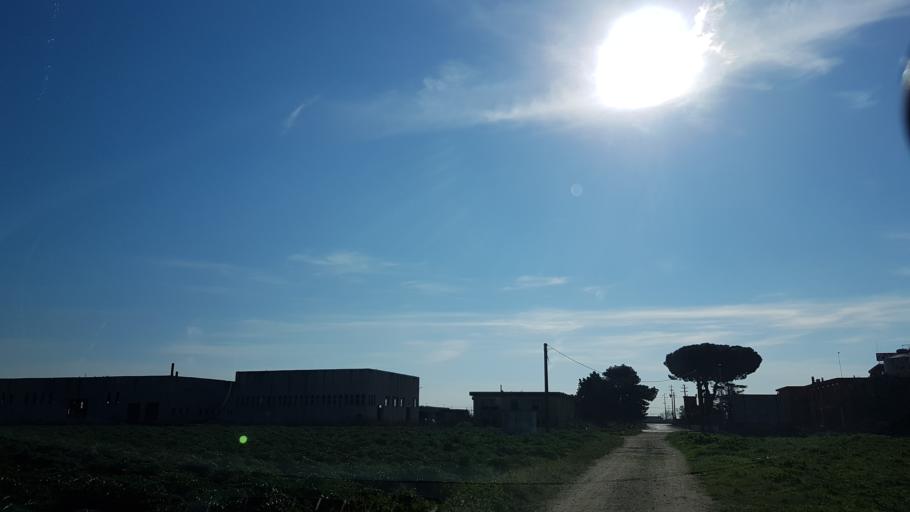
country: IT
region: Apulia
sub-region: Provincia di Brindisi
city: Brindisi
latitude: 40.6101
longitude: 17.8865
